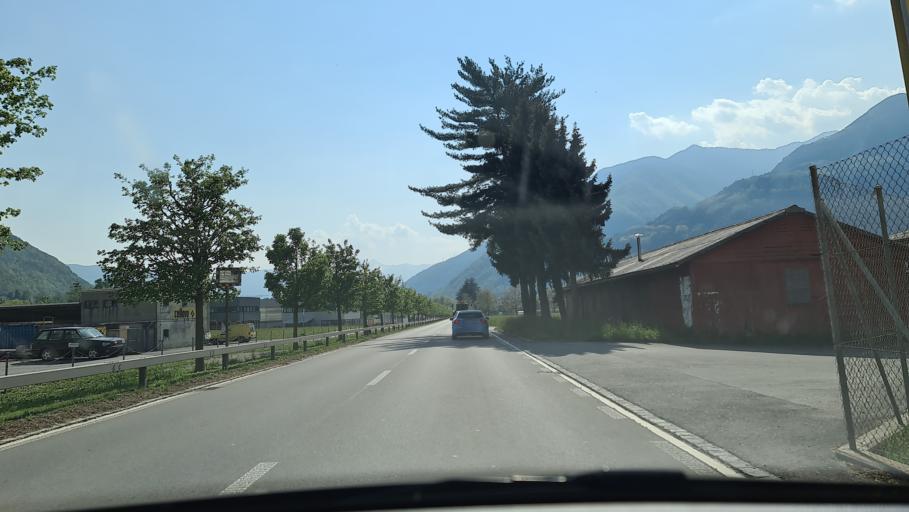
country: CH
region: Ticino
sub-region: Bellinzona District
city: Lumino
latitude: 46.2273
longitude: 9.0573
